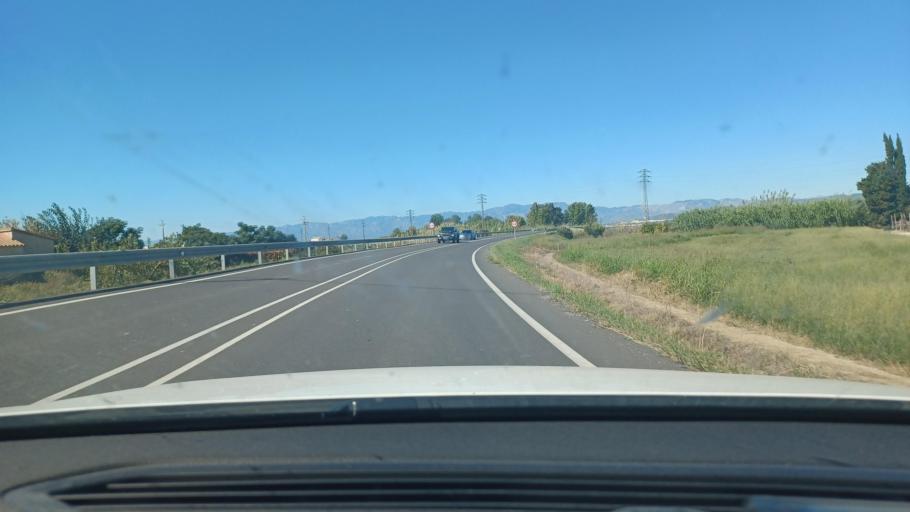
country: ES
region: Catalonia
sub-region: Provincia de Tarragona
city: Deltebre
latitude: 40.7284
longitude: 0.6880
